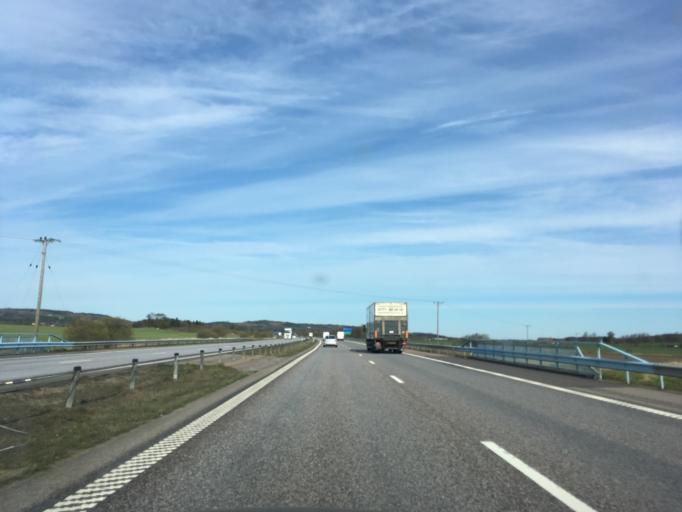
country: SE
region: Halland
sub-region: Halmstads Kommun
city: Getinge
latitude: 56.8001
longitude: 12.7704
